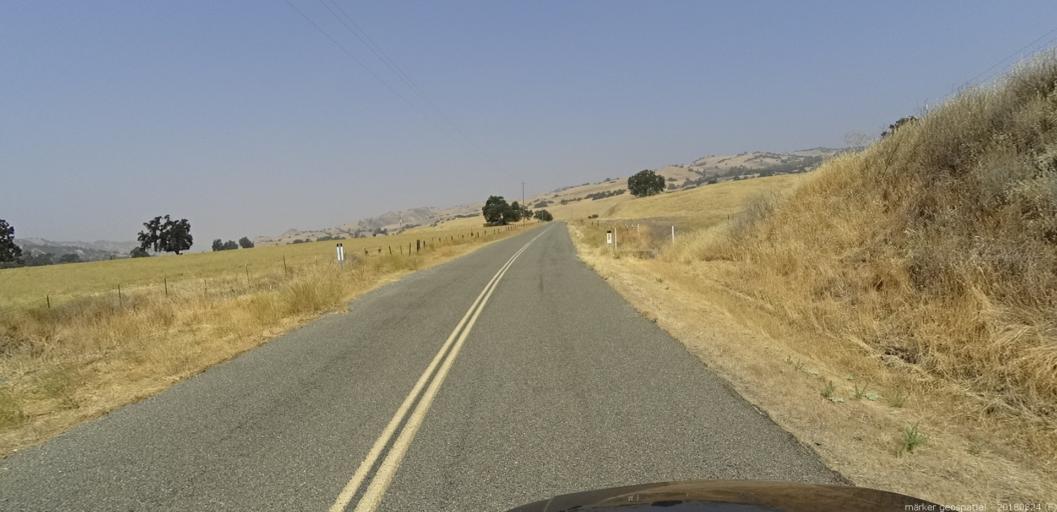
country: US
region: California
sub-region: Monterey County
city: King City
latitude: 36.1772
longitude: -120.7962
